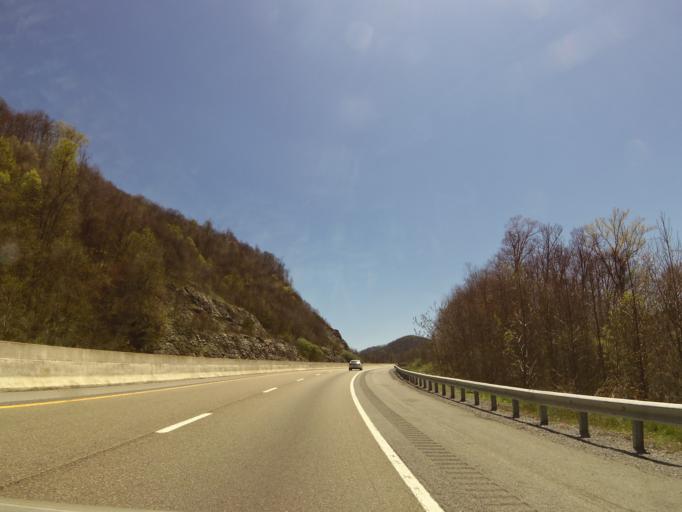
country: US
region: North Carolina
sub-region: Madison County
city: Mars Hill
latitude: 35.9699
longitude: -82.5519
